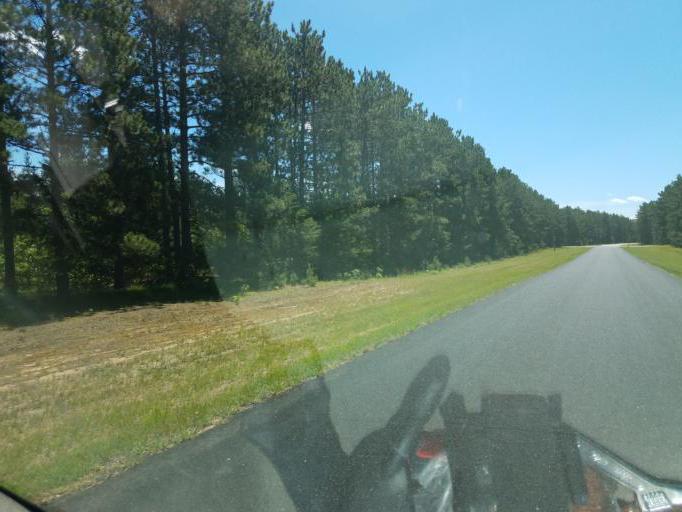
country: US
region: Wisconsin
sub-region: Juneau County
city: New Lisbon
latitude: 44.0483
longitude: -90.0274
